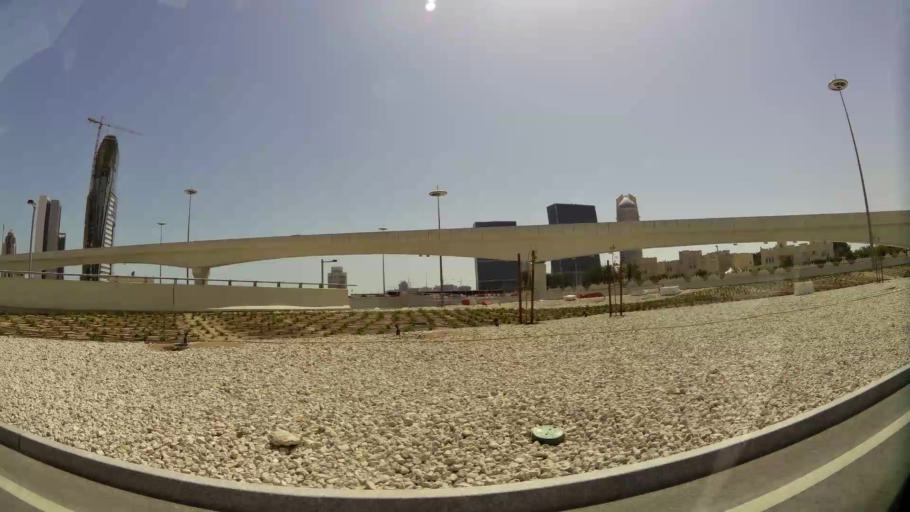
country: QA
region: Baladiyat ad Dawhah
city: Doha
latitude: 25.3818
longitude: 51.5194
